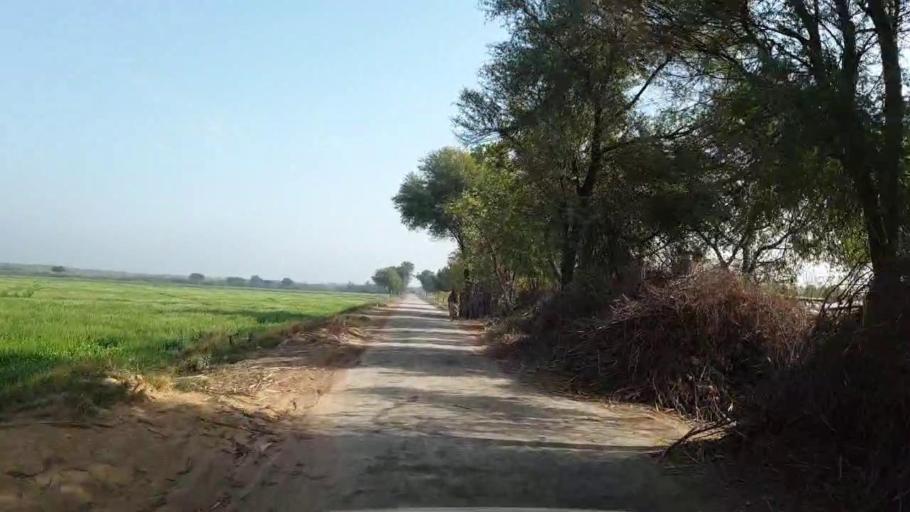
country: PK
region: Sindh
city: Matiari
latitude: 25.5951
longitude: 68.4869
